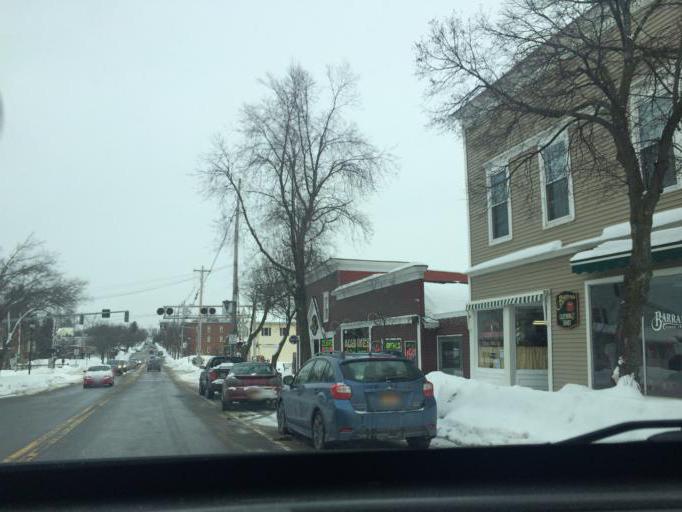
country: US
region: New York
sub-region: Monroe County
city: Fairport
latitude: 43.1026
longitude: -77.4419
